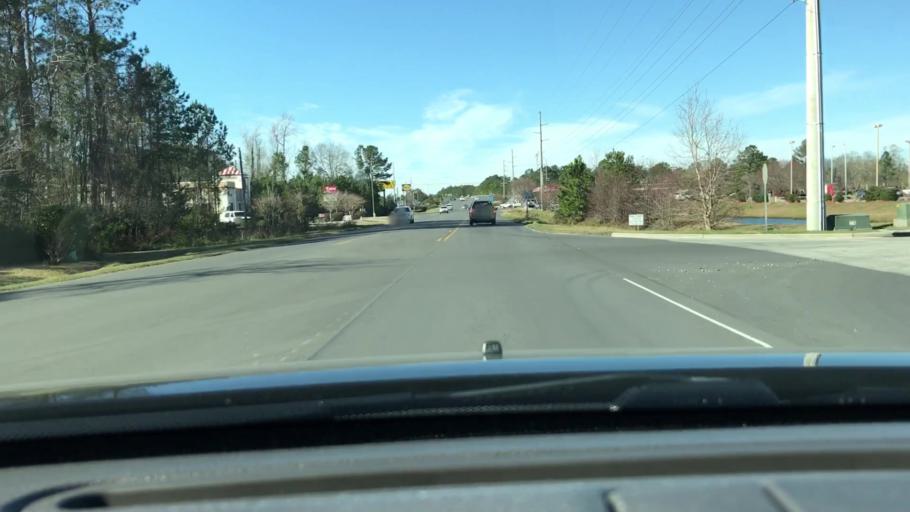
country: US
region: North Carolina
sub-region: Brunswick County
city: Shallotte
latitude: 33.9730
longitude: -78.3994
